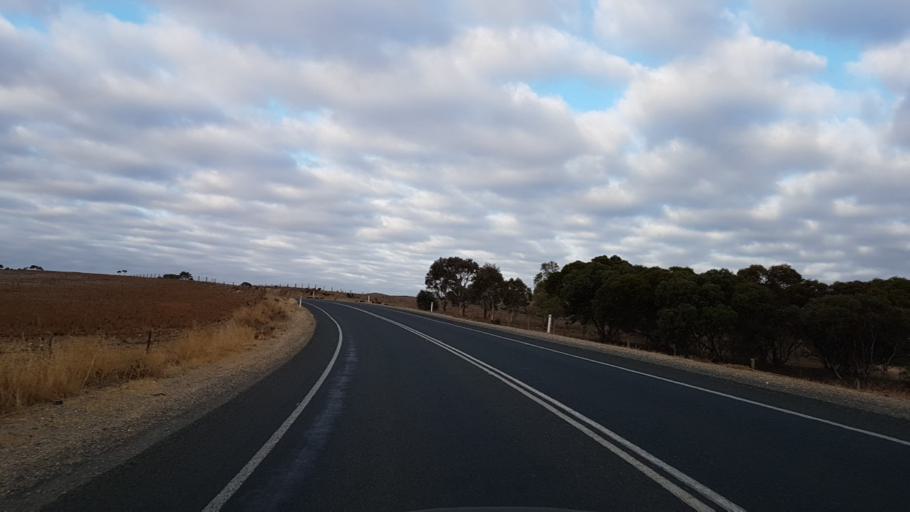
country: AU
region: South Australia
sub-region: Mount Barker
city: Callington
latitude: -35.1356
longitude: 139.0298
